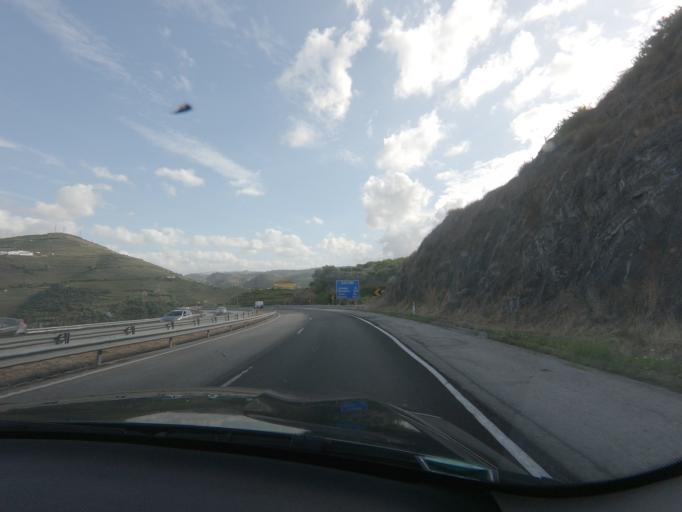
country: PT
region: Vila Real
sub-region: Peso da Regua
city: Peso da Regua
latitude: 41.1615
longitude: -7.7727
